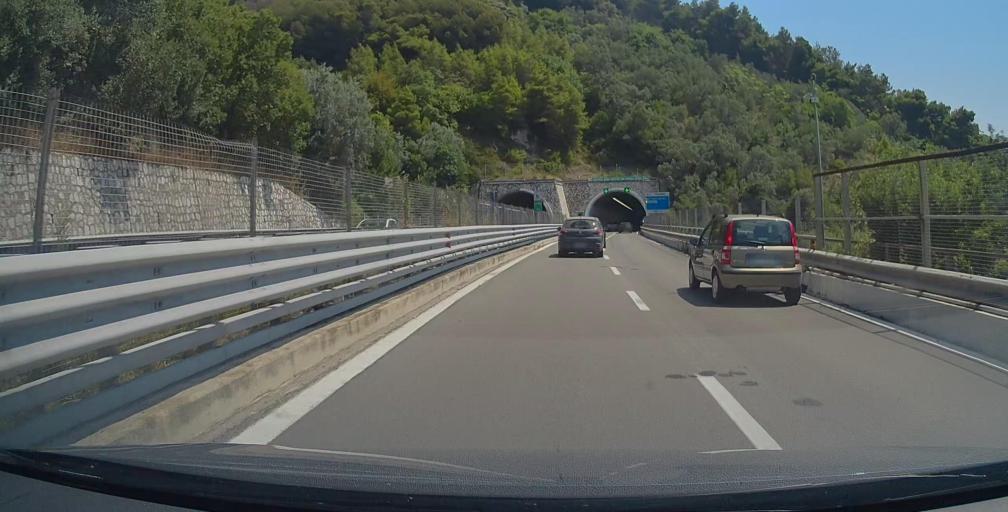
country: IT
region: Campania
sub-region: Provincia di Salerno
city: Capezzano Inferiore
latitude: 40.6827
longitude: 14.7517
